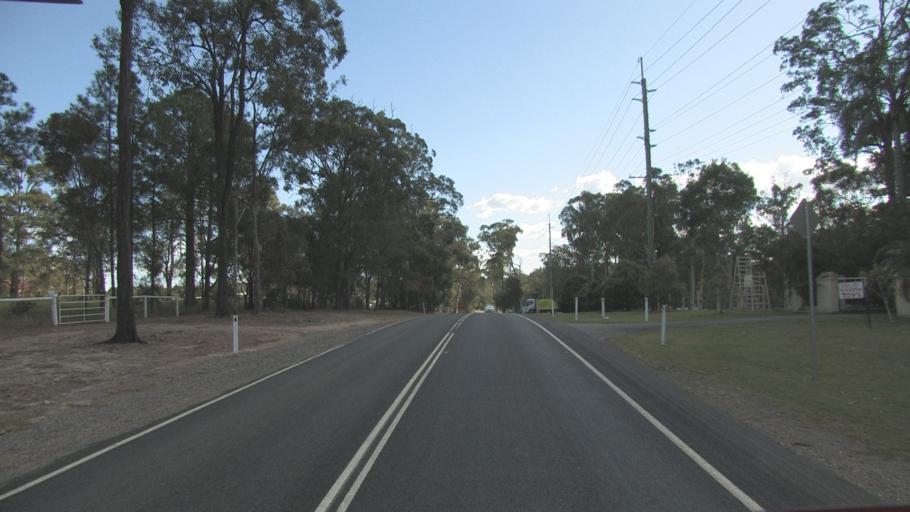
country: AU
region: Queensland
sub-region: Logan
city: Beenleigh
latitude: -27.6568
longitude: 153.2258
